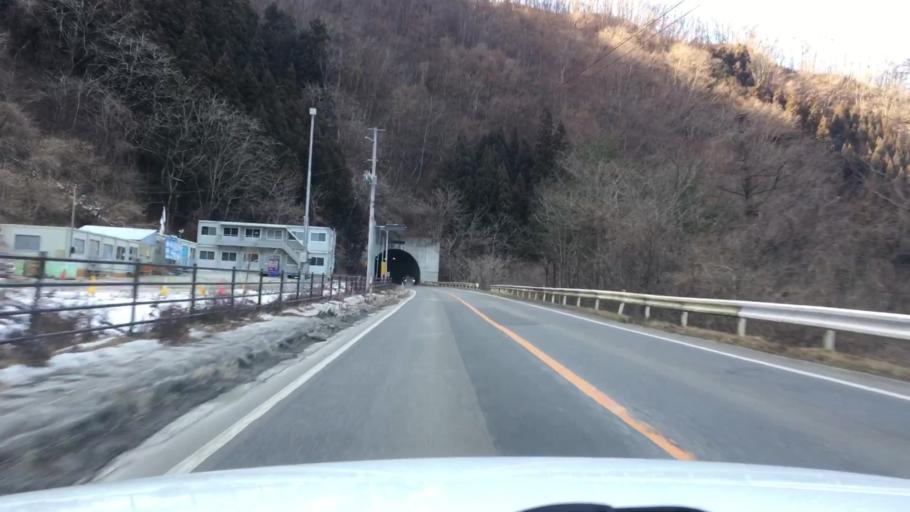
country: JP
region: Iwate
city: Tono
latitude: 39.6207
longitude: 141.6205
